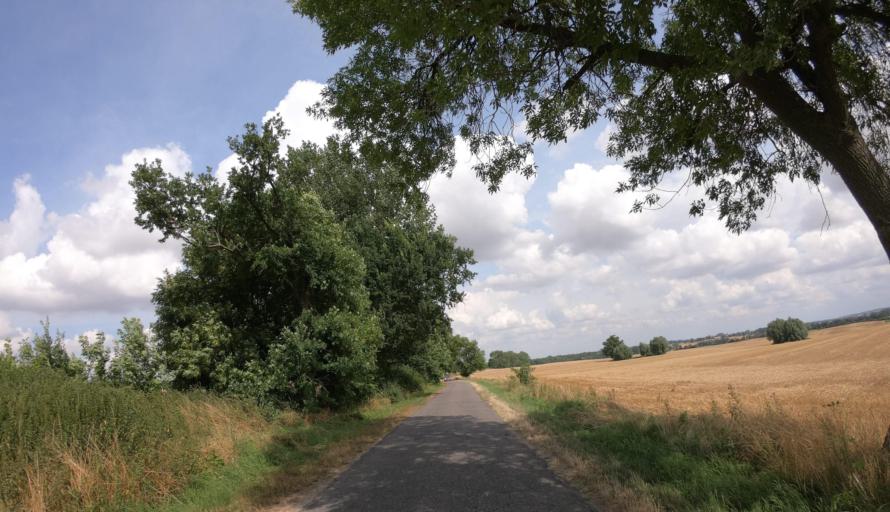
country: PL
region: West Pomeranian Voivodeship
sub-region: Powiat pyrzycki
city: Kozielice
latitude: 53.0583
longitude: 14.8925
